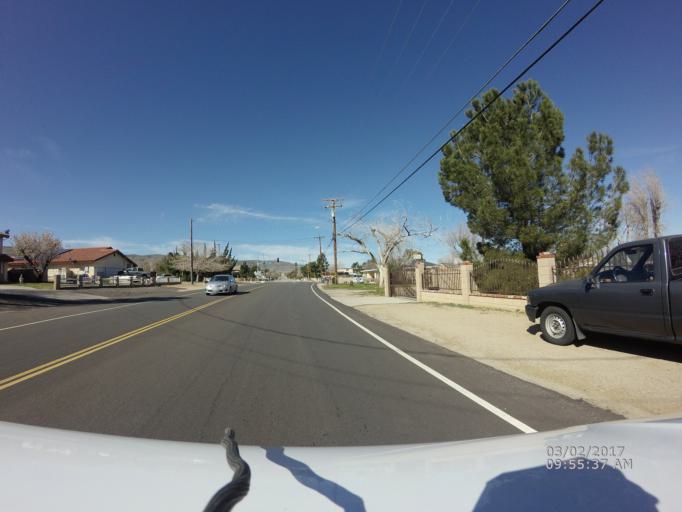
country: US
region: California
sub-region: Los Angeles County
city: Quartz Hill
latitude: 34.6383
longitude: -118.2177
